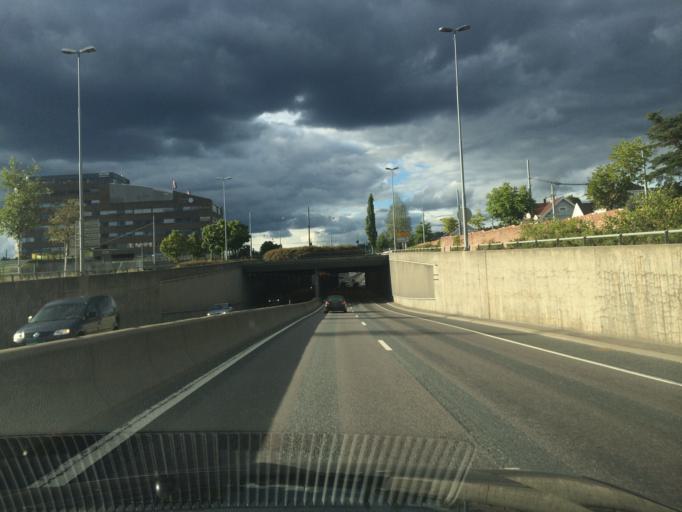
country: NO
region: Oslo
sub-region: Oslo
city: Oslo
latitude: 59.9440
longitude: 10.7800
